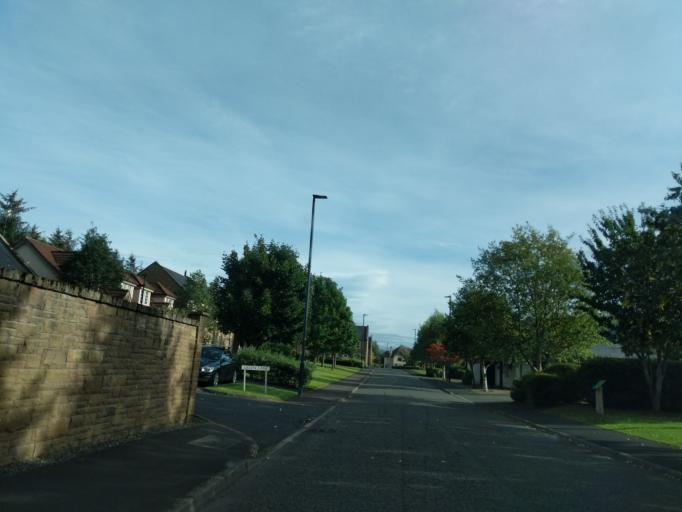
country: GB
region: Scotland
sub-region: The Scottish Borders
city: Innerleithen
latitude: 55.6382
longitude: -3.1056
